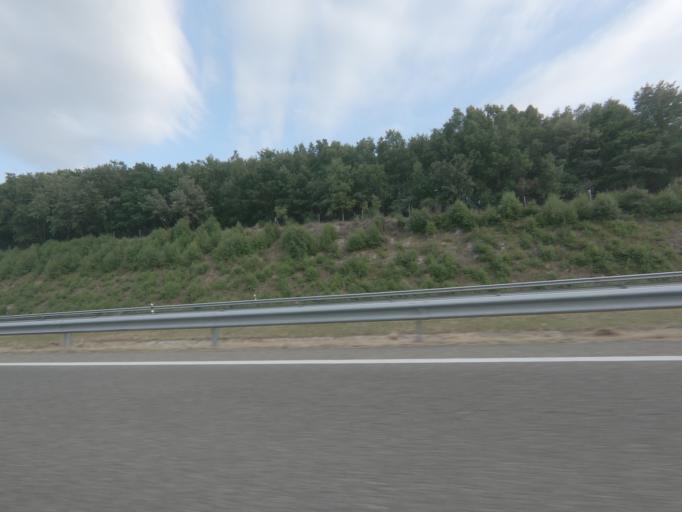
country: ES
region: Galicia
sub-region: Provincia de Ourense
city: Allariz
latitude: 42.2027
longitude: -7.7947
